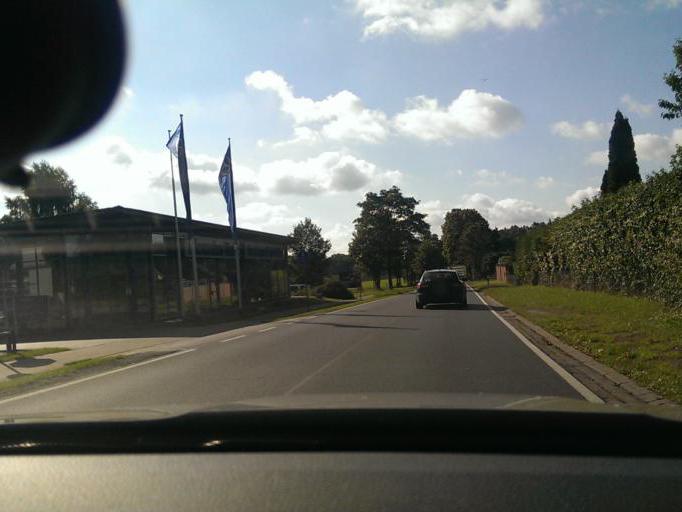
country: DE
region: Lower Saxony
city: Elze
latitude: 52.5421
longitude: 9.7407
